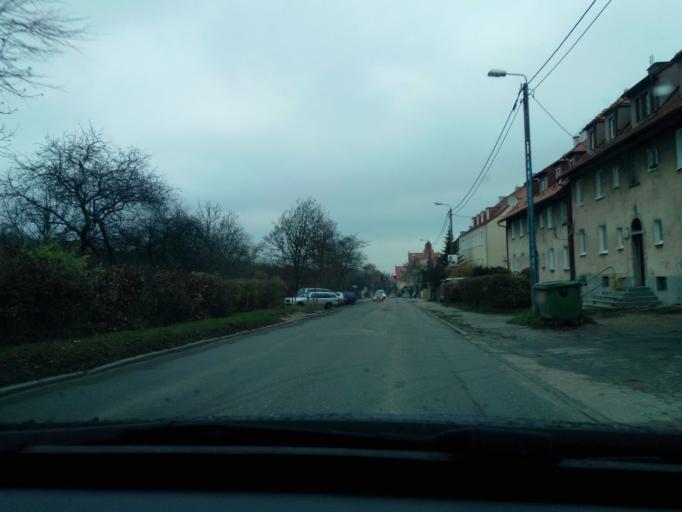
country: PL
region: Pomeranian Voivodeship
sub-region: Gdansk
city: Gdansk
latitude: 54.3629
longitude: 18.6115
